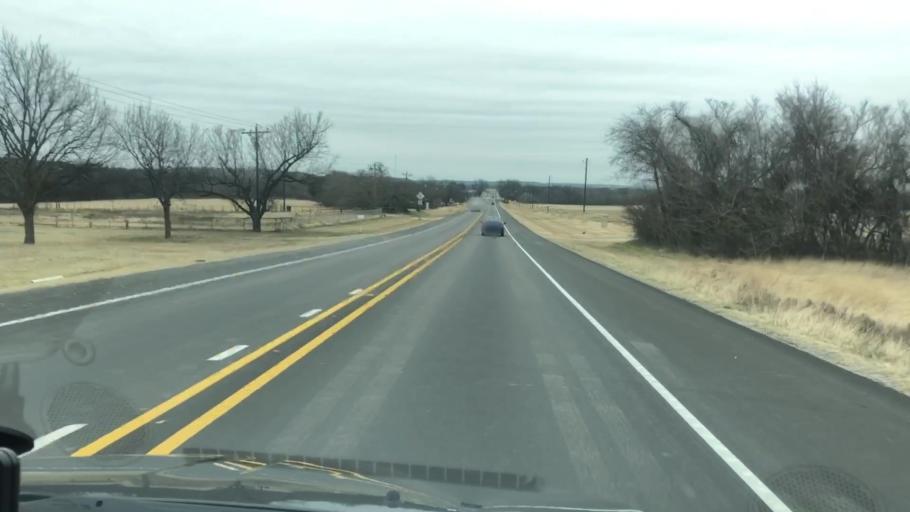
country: US
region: Texas
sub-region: Erath County
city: Stephenville
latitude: 32.3702
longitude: -98.1748
